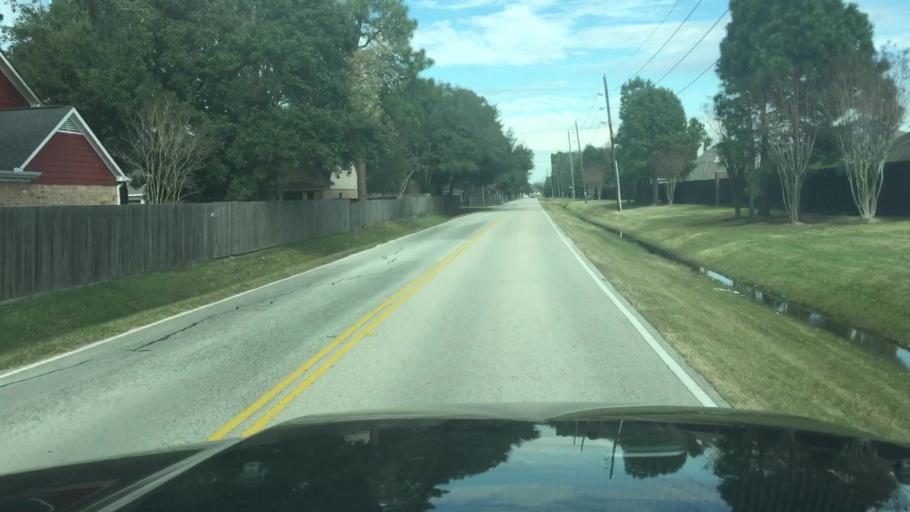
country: US
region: Texas
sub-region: Harris County
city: Oak Cliff Place
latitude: 29.8411
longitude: -95.6752
